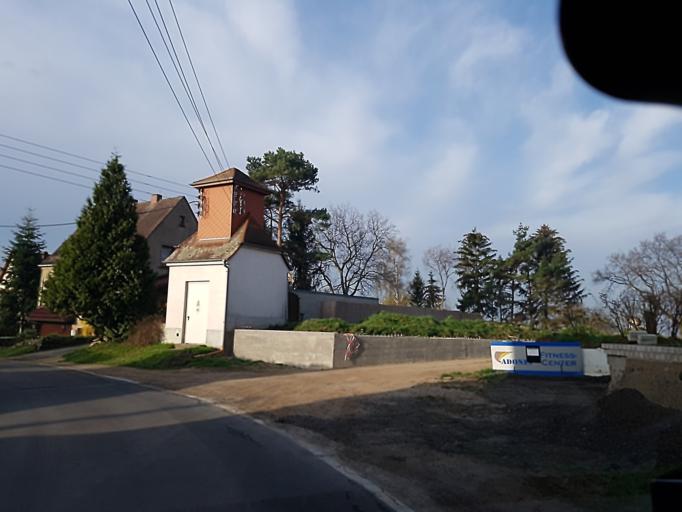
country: DE
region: Saxony
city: Stauchitz
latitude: 51.2711
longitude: 13.1961
